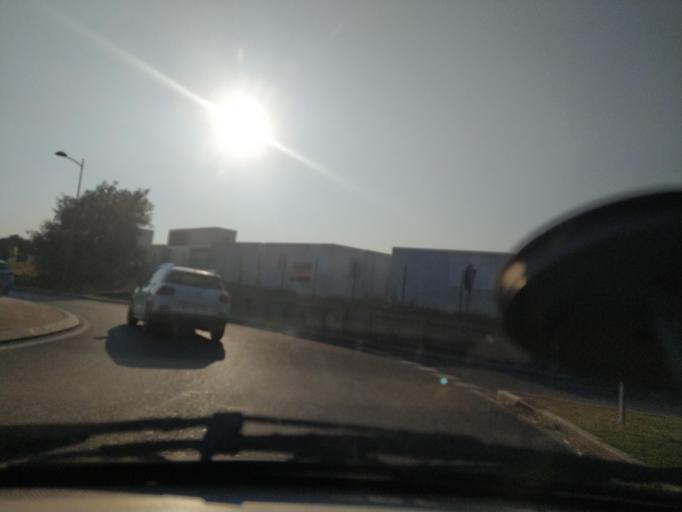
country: FR
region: Aquitaine
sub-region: Departement des Landes
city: Saint-Geours-de-Maremne
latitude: 43.6844
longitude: -1.2385
